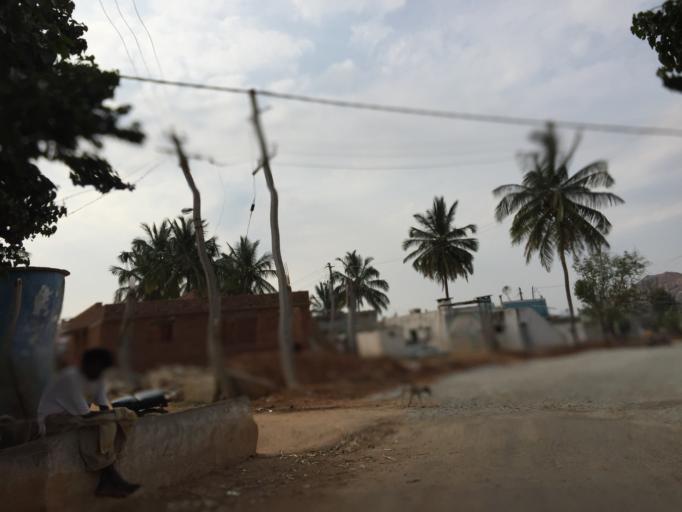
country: IN
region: Karnataka
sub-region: Chikkaballapur
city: Gudibanda
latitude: 13.5677
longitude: 77.7309
